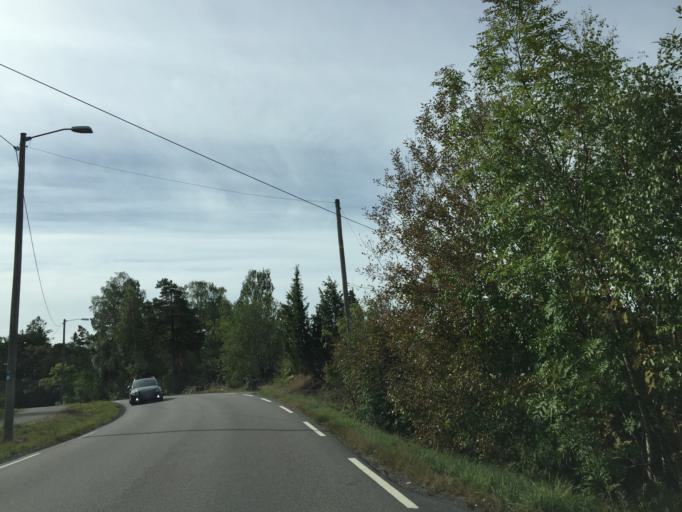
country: NO
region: Ostfold
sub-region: Moss
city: Moss
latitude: 59.5071
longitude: 10.6853
